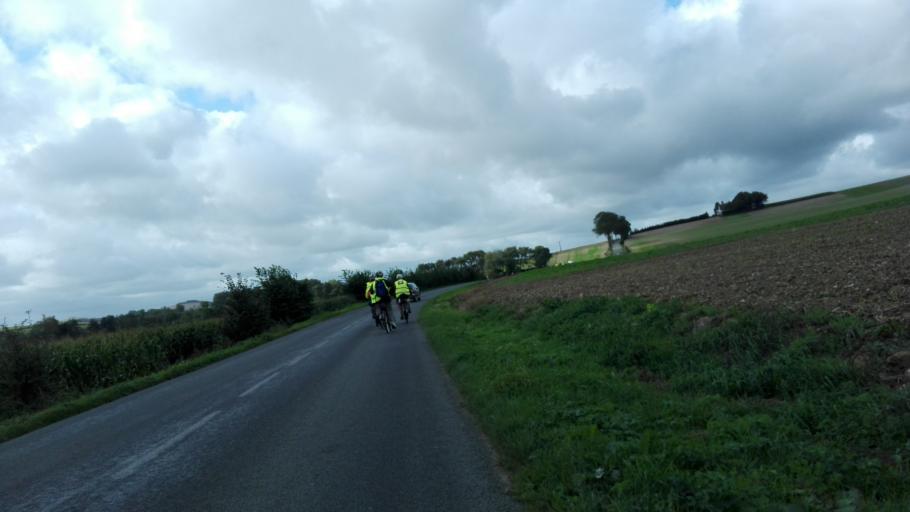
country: FR
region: Nord-Pas-de-Calais
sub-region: Departement du Pas-de-Calais
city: Licques
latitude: 50.7893
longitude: 1.9797
